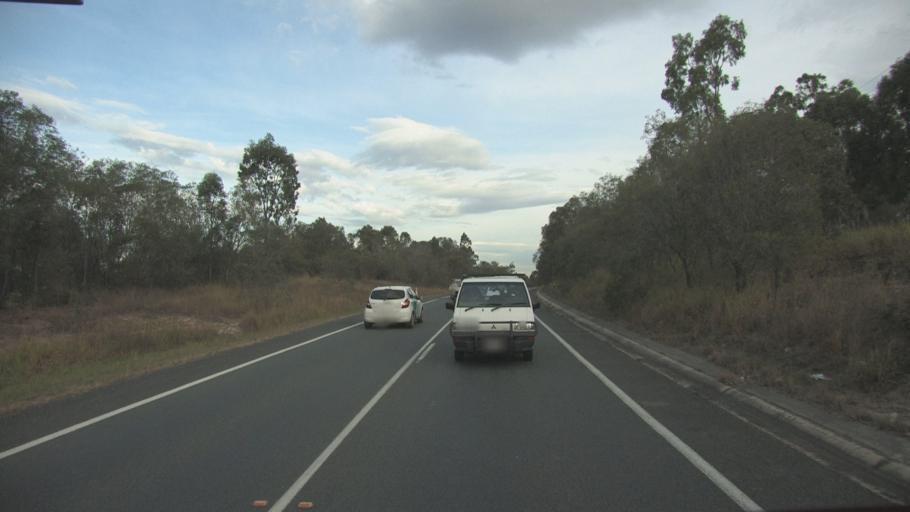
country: AU
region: Queensland
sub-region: Logan
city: Chambers Flat
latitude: -27.8329
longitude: 153.1068
